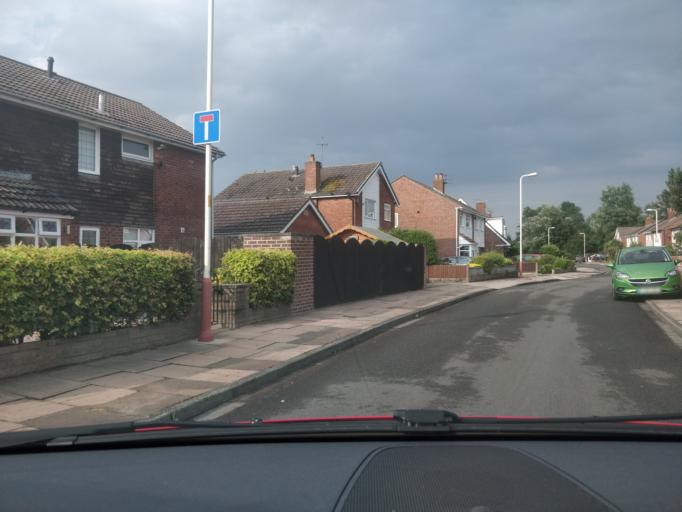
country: GB
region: England
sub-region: Lancashire
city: Banks
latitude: 53.6754
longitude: -2.9588
